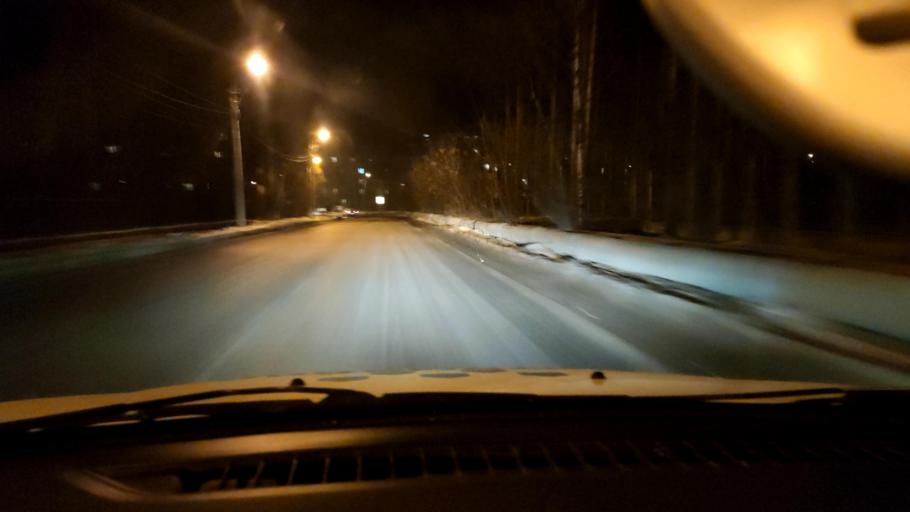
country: RU
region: Perm
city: Overyata
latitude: 58.0257
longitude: 55.8458
